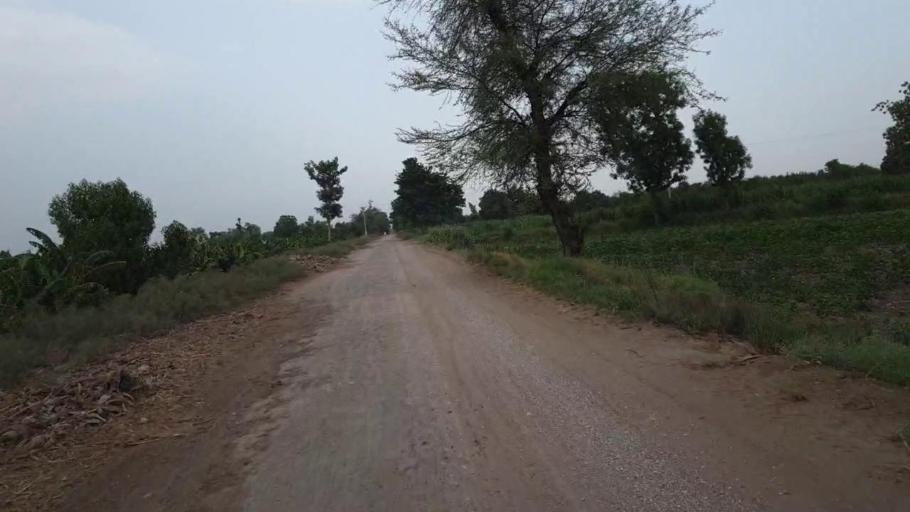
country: PK
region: Sindh
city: Bandhi
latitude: 26.5297
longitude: 68.1967
